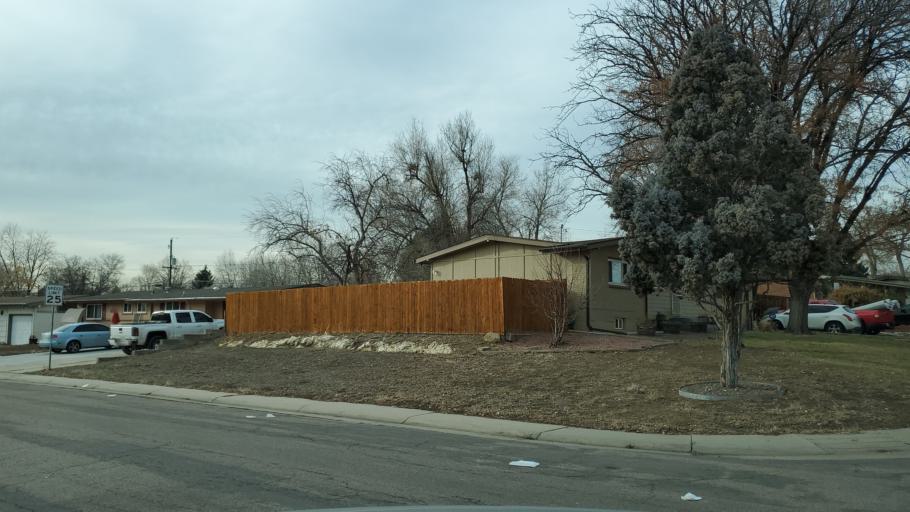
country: US
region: Colorado
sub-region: Adams County
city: Westminster
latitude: 39.8408
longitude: -105.0201
